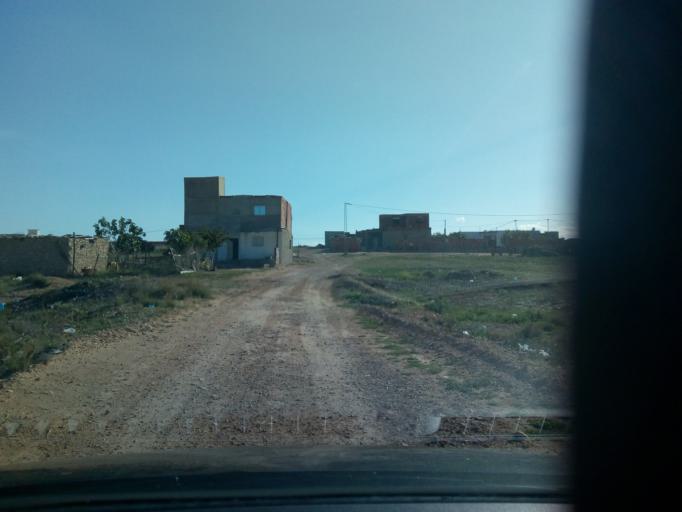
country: TN
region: Safaqis
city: Sfax
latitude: 34.7224
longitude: 10.6115
